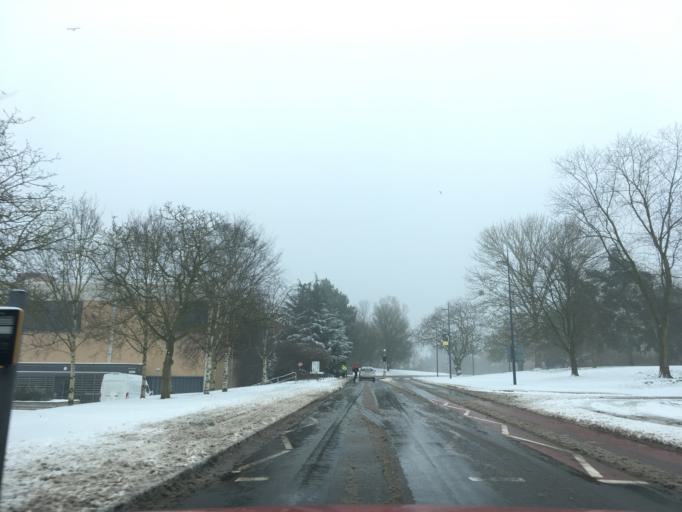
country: GB
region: England
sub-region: Warwickshire
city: Kenilworth
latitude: 52.3818
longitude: -1.5597
